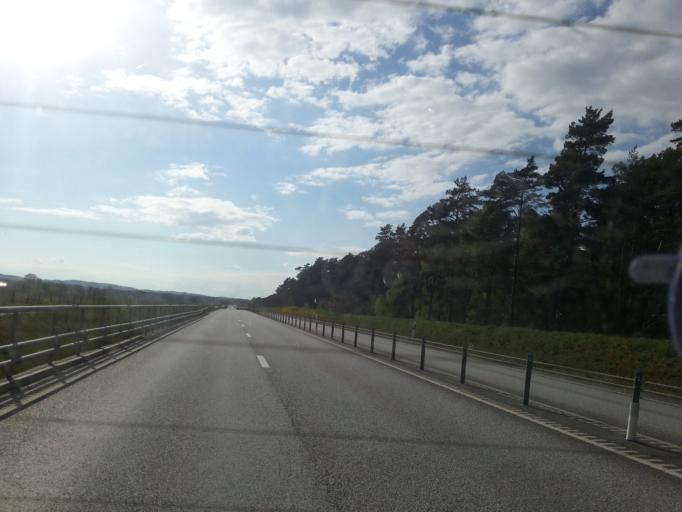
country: SE
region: Skane
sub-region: Sjobo Kommun
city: Blentarp
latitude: 55.6390
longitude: 13.5630
